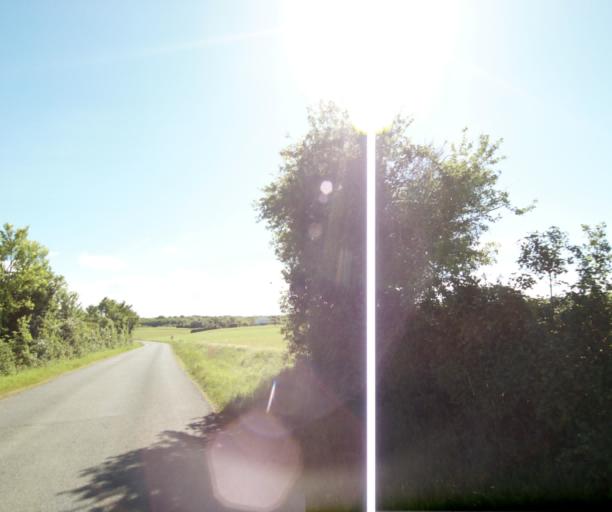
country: FR
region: Poitou-Charentes
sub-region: Departement de la Charente-Maritime
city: Bussac-sur-Charente
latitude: 45.8163
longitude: -0.6613
